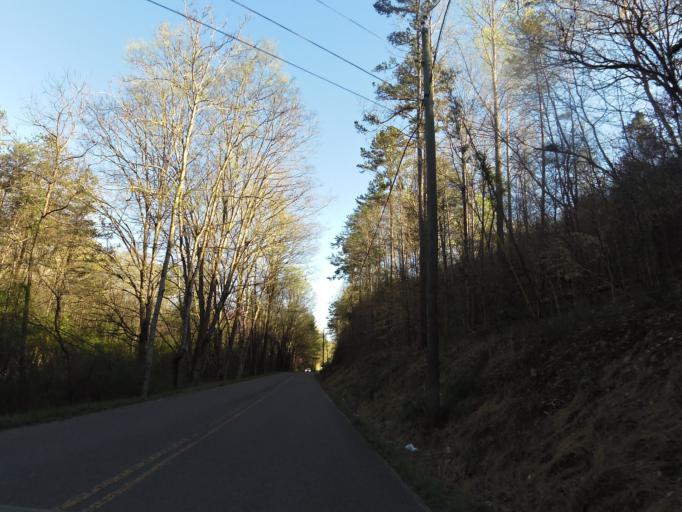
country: US
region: Tennessee
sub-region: Knox County
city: Mascot
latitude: 35.9895
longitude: -83.7598
